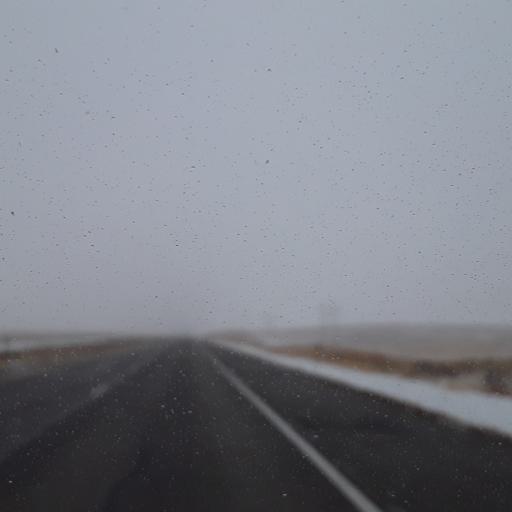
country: US
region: Nebraska
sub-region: Cheyenne County
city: Sidney
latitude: 40.7944
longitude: -102.8818
